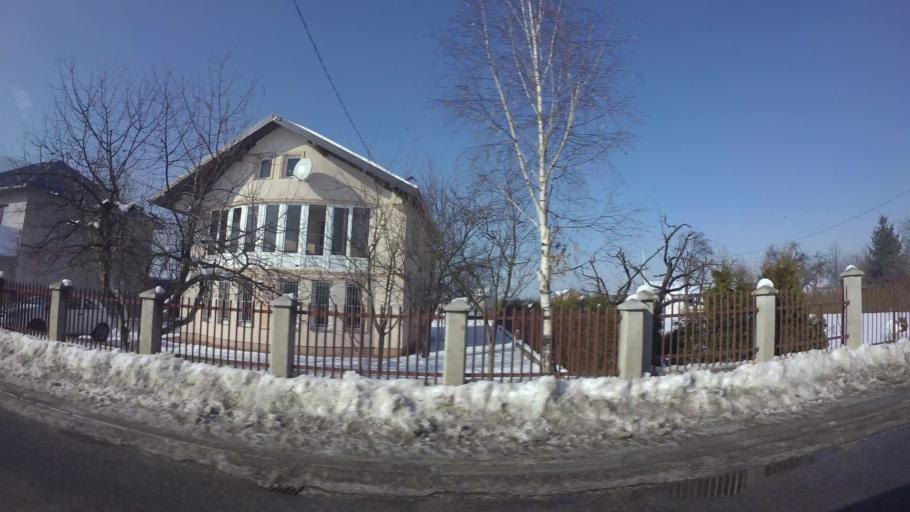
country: BA
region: Federation of Bosnia and Herzegovina
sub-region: Kanton Sarajevo
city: Sarajevo
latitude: 43.8109
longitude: 18.3025
